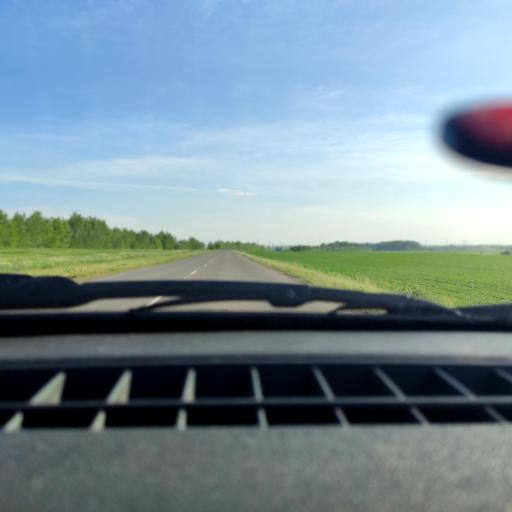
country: RU
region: Bashkortostan
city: Avdon
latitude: 54.4428
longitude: 55.8400
